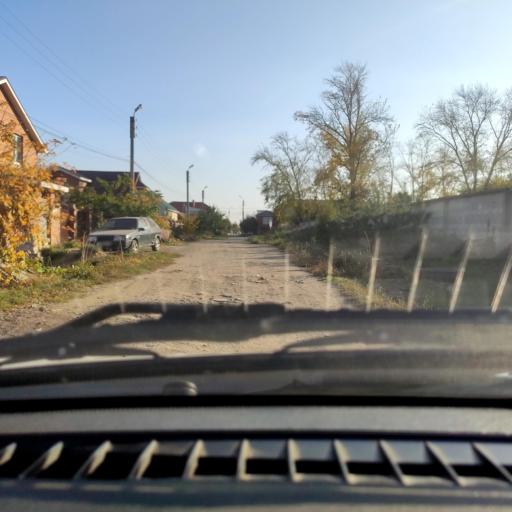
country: RU
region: Samara
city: Tol'yatti
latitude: 53.5357
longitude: 49.4054
